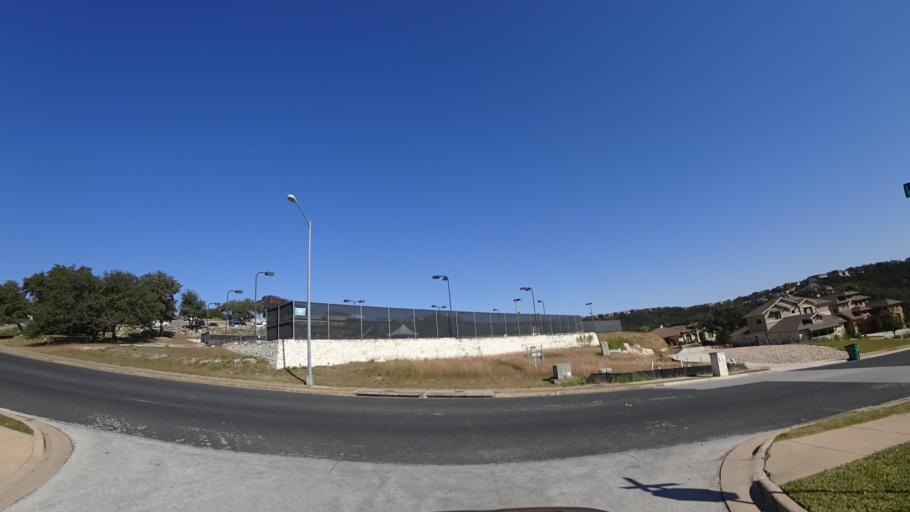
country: US
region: Texas
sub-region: Travis County
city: Lost Creek
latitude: 30.3669
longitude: -97.8615
